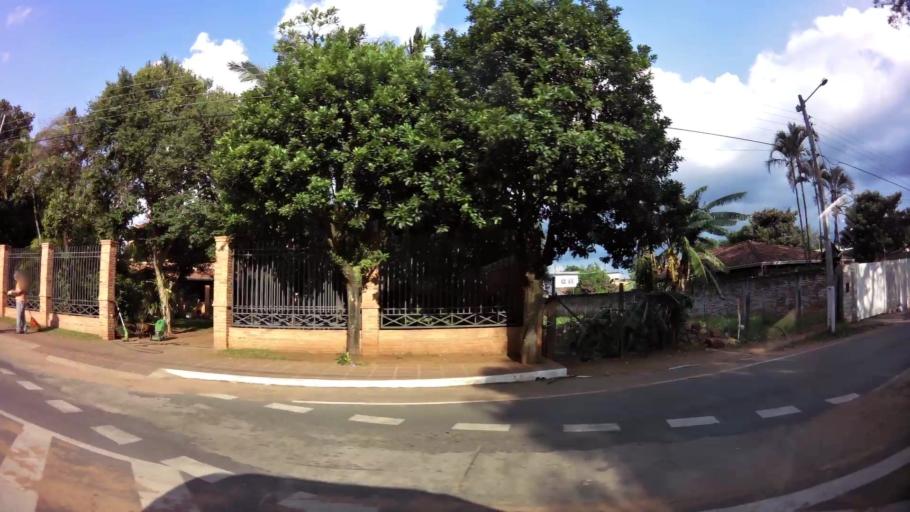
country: PY
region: Central
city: Fernando de la Mora
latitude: -25.3483
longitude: -57.5526
